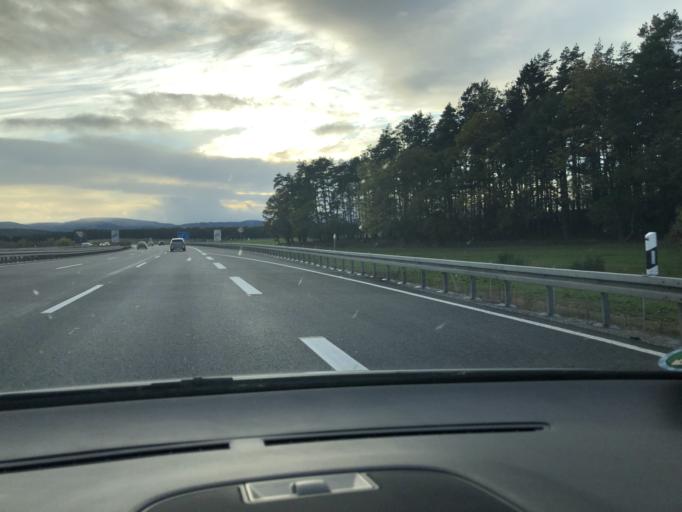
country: DE
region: Thuringia
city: Behringen
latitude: 50.7465
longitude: 10.9953
